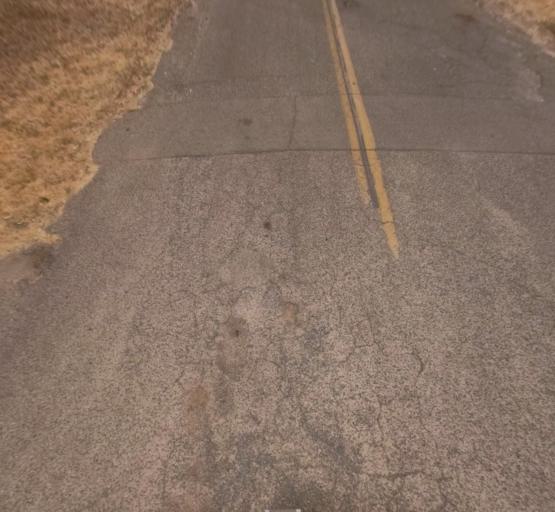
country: US
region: California
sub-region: Madera County
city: Madera Acres
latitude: 37.0026
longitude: -120.0677
